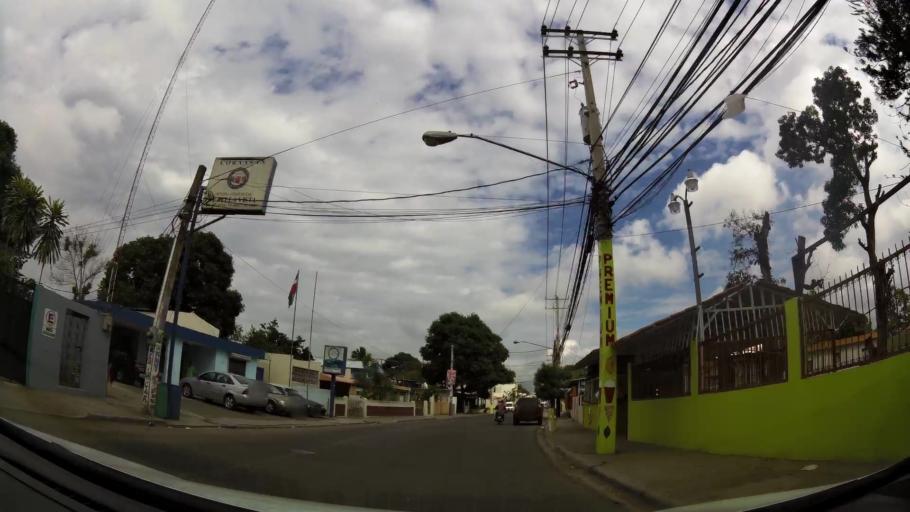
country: DO
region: Santiago
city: Santiago de los Caballeros
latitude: 19.4409
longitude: -70.7069
